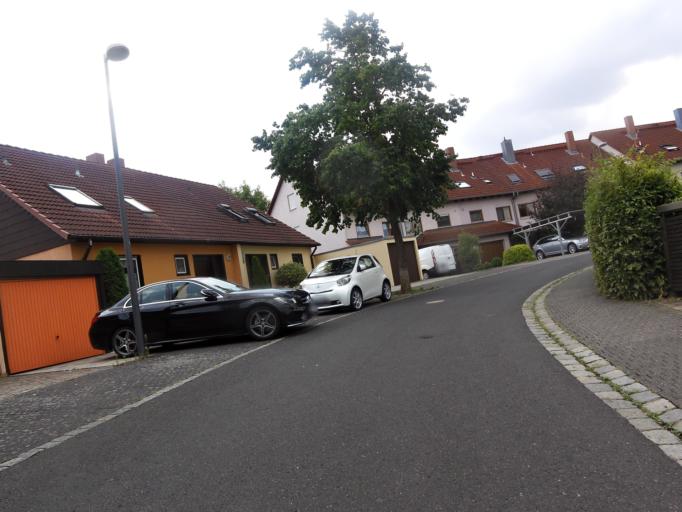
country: DE
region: Bavaria
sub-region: Regierungsbezirk Unterfranken
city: Randersacker
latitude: 49.7377
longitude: 9.9648
